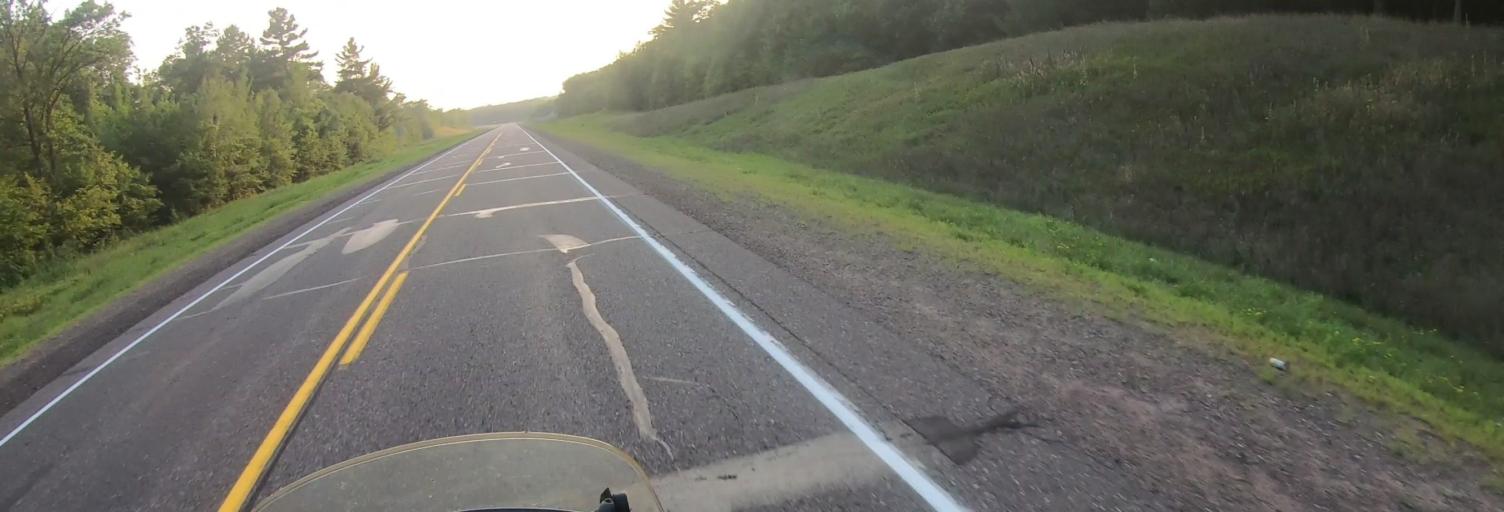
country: US
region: Wisconsin
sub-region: Burnett County
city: Siren
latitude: 45.7767
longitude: -92.4386
